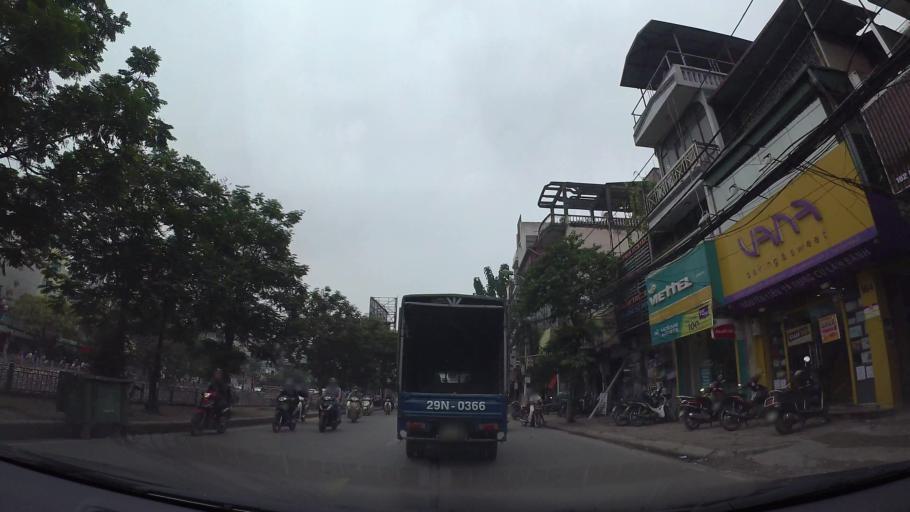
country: VN
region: Ha Noi
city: Hai BaTrung
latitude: 21.0037
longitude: 105.8612
